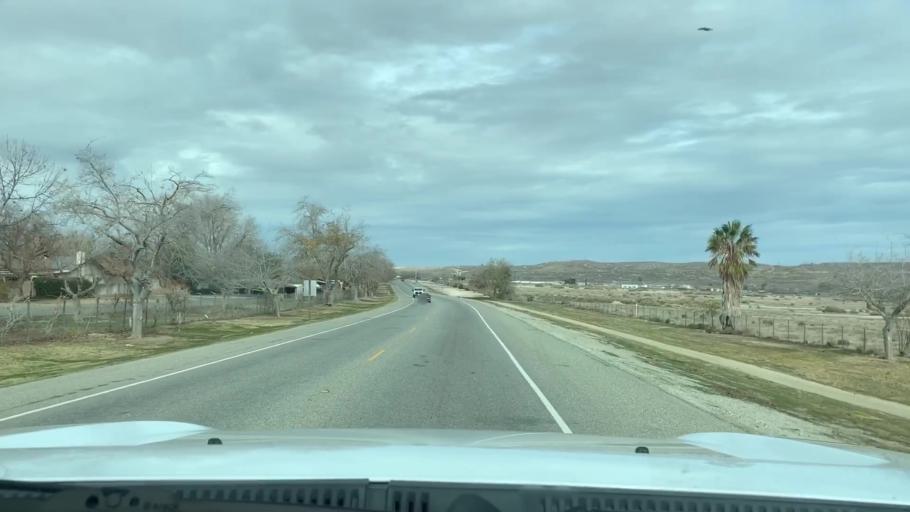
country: US
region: California
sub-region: Kern County
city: Taft
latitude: 35.1440
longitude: -119.4472
